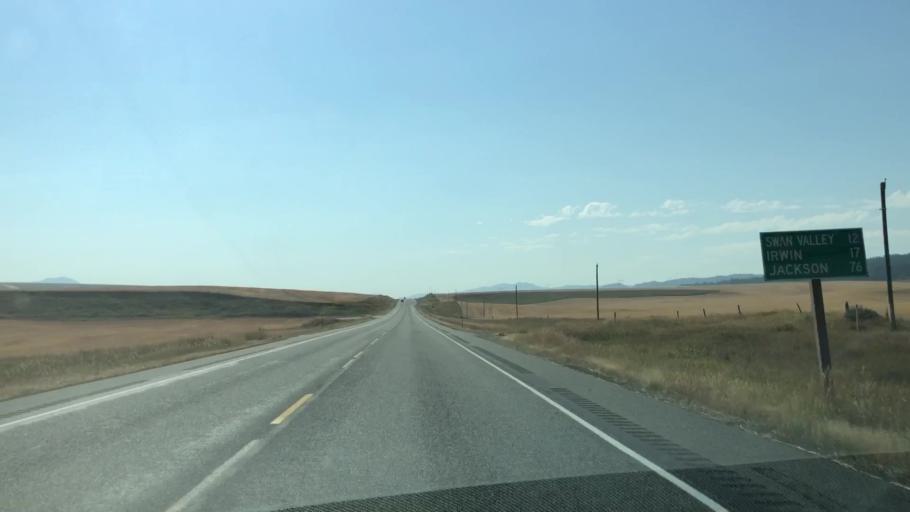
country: US
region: Idaho
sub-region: Madison County
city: Rexburg
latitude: 43.5356
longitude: -111.5110
